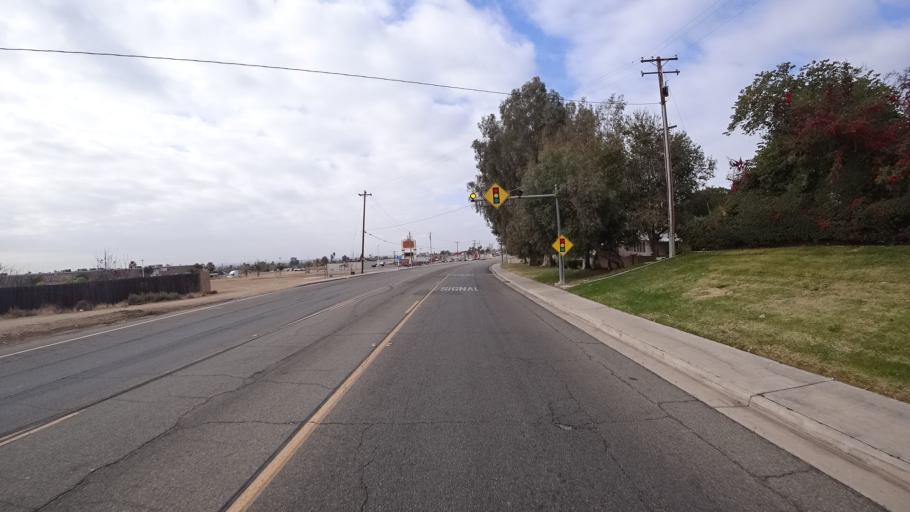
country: US
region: California
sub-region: Kern County
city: Bakersfield
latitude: 35.3764
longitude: -118.9113
